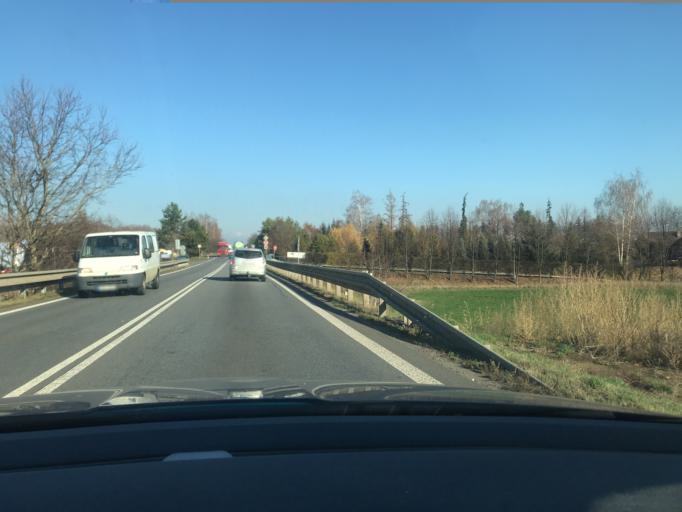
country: CZ
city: Predmerice nad Labem
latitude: 50.2427
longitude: 15.7973
